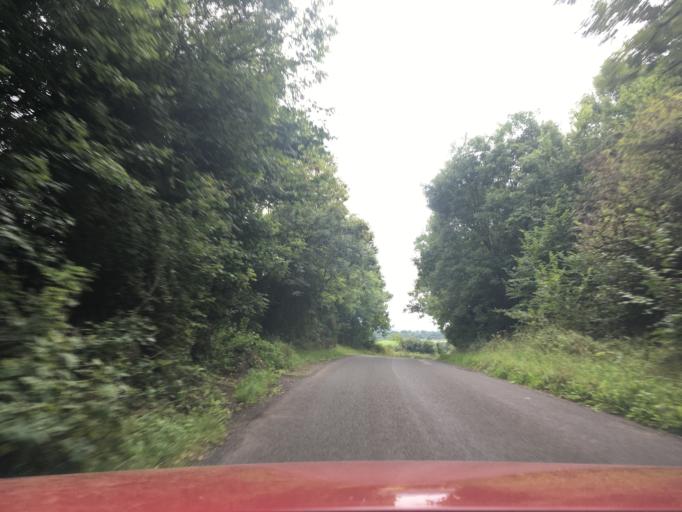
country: GB
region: England
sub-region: South Gloucestershire
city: Tytherington
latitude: 51.5854
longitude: -2.4985
